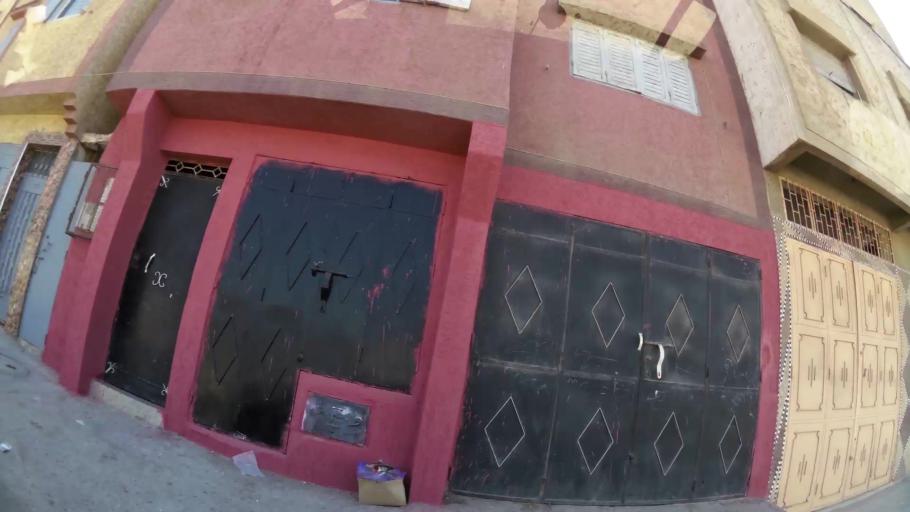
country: MA
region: Rabat-Sale-Zemmour-Zaer
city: Sale
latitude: 34.0611
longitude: -6.7783
